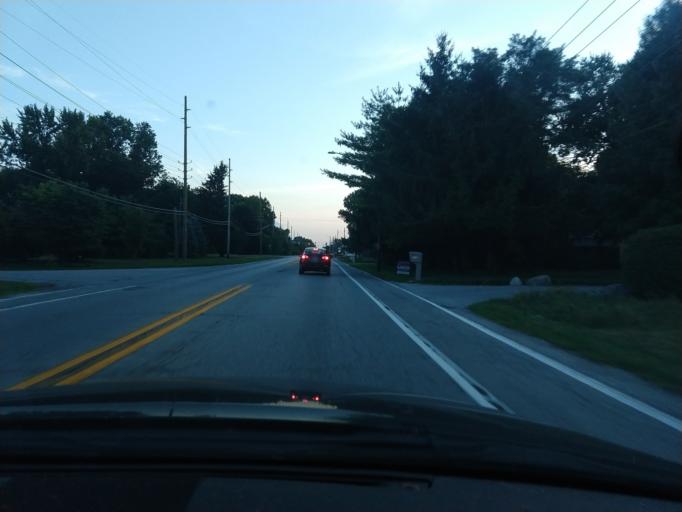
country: US
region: Indiana
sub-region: Marion County
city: Broad Ripple
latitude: 39.8495
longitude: -86.1093
